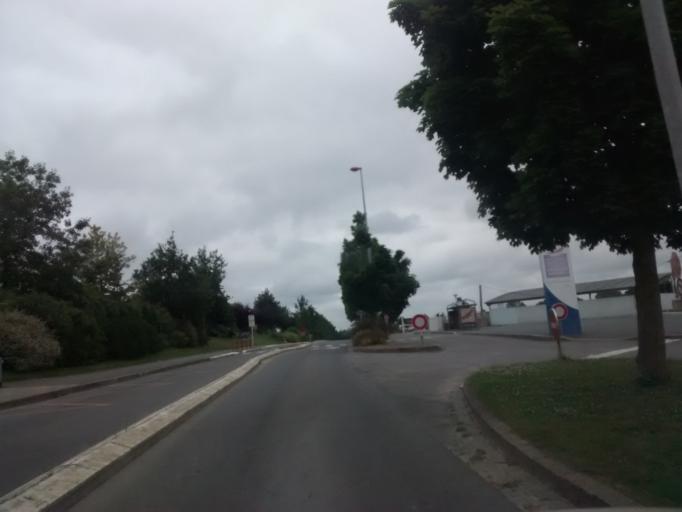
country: FR
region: Brittany
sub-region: Departement d'Ille-et-Vilaine
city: Saint-Gregoire
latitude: 48.1599
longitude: -1.6771
